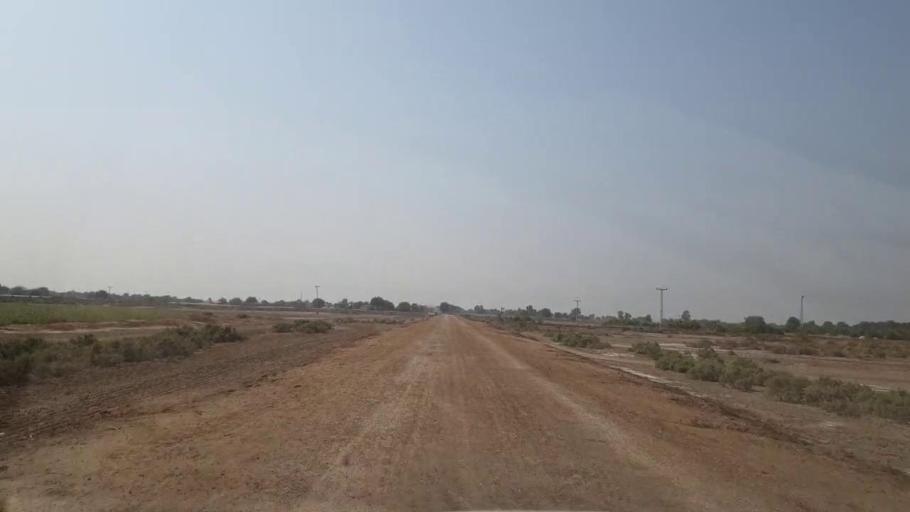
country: PK
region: Sindh
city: Mirpur Khas
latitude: 25.6375
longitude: 69.1451
